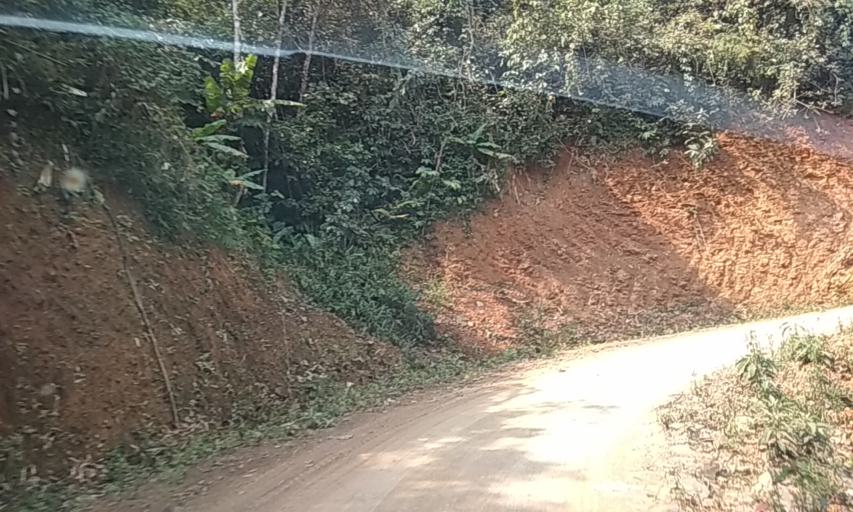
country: LA
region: Phongsali
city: Phongsali
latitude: 21.4645
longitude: 102.4222
